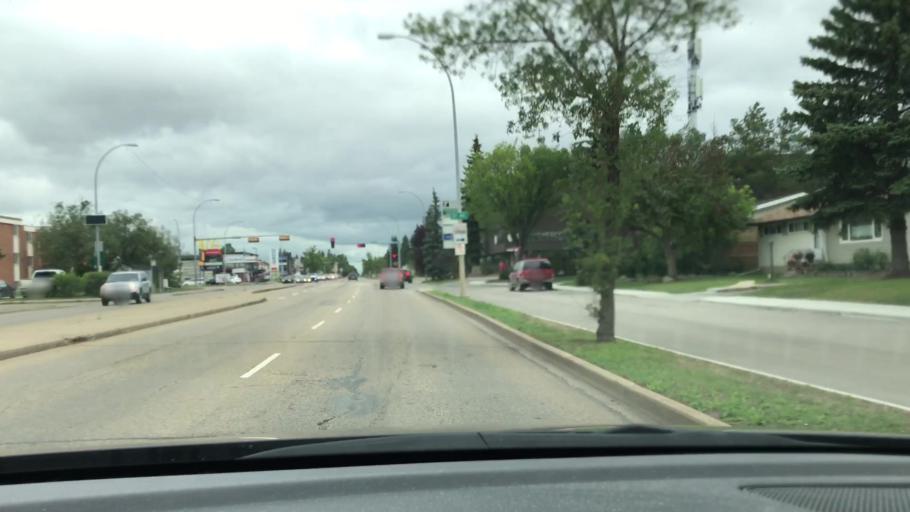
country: CA
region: Alberta
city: Edmonton
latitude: 53.5183
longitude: -113.5778
